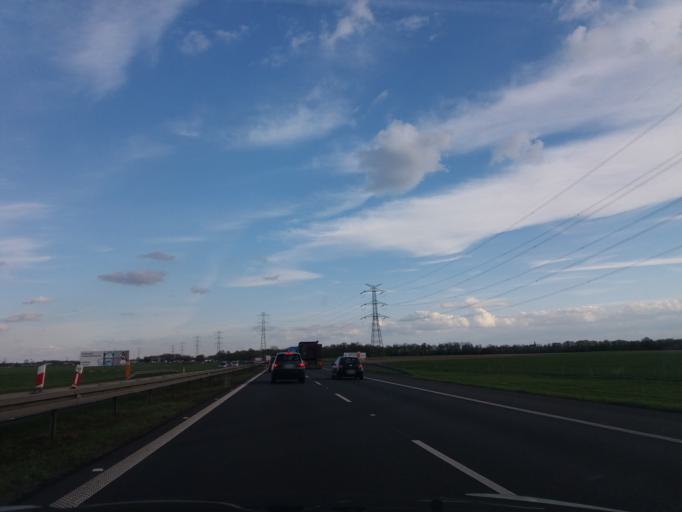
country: PL
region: Opole Voivodeship
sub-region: Powiat brzeski
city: Skarbimierz Osiedle
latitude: 50.7957
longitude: 17.3272
